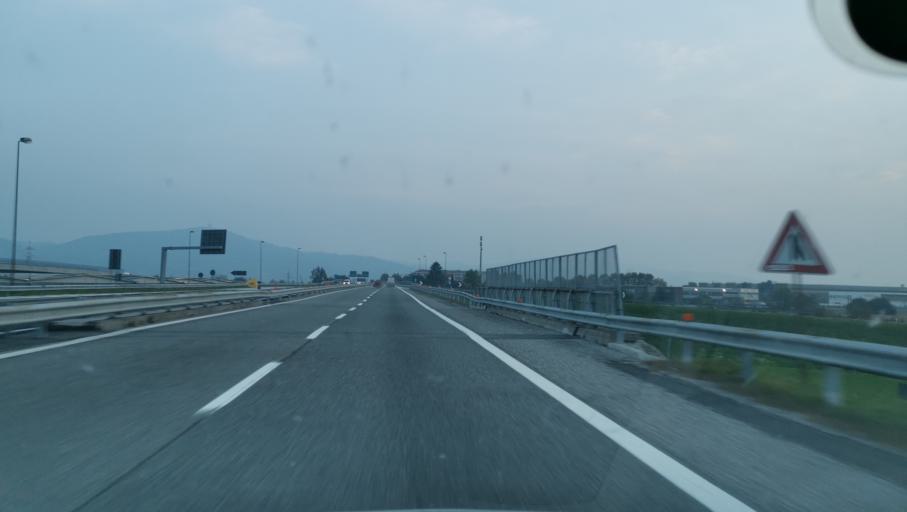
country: IT
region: Piedmont
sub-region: Provincia di Torino
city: Settimo Torinese
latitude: 45.1305
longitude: 7.7298
